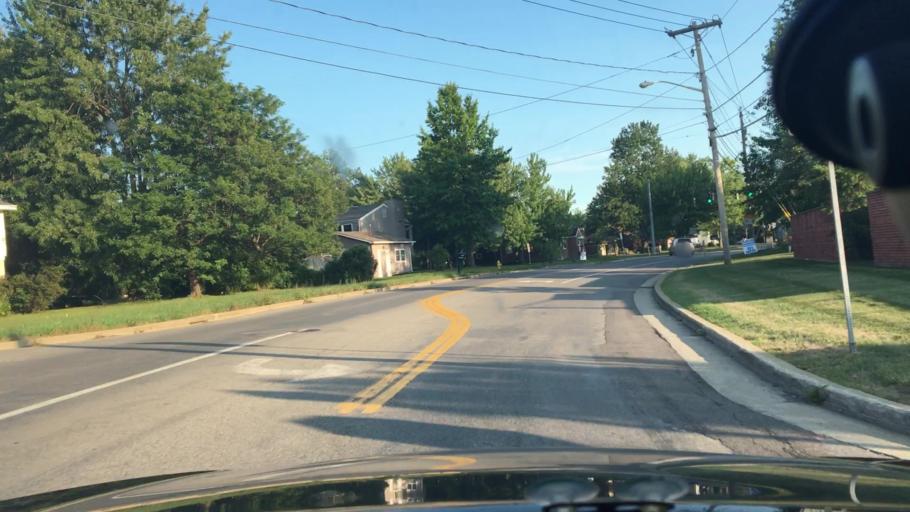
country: US
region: New York
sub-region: Erie County
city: Williamsville
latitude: 43.0029
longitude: -78.7609
